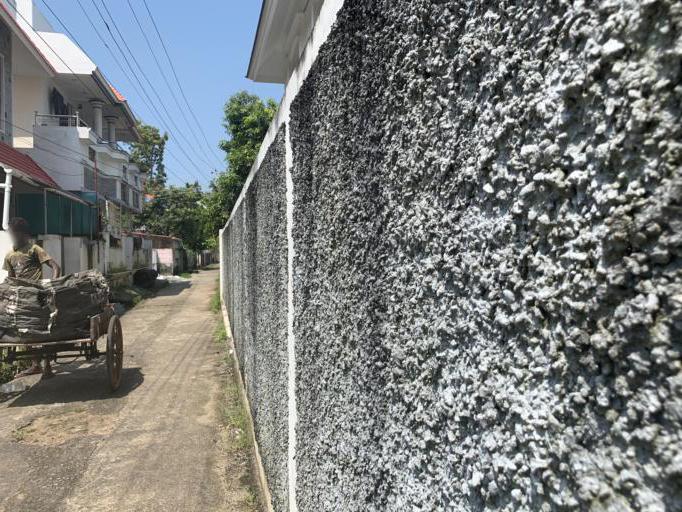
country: IN
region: Kerala
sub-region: Ernakulam
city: Cochin
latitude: 9.9766
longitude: 76.2410
